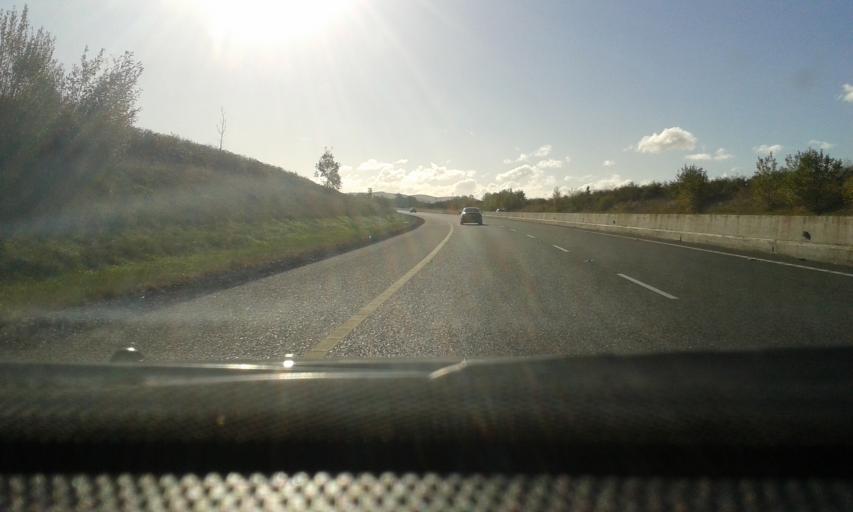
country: IE
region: Leinster
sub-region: Laois
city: Rathdowney
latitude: 52.8386
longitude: -7.5013
